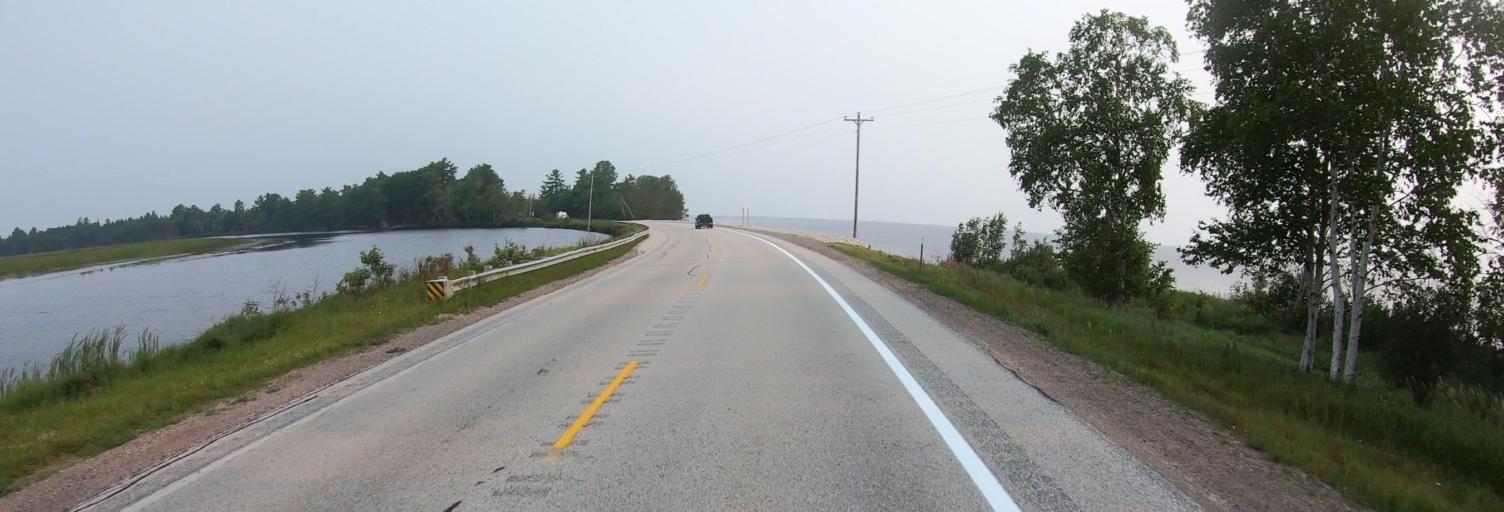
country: US
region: Michigan
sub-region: Luce County
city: Newberry
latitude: 46.5596
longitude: -85.0291
